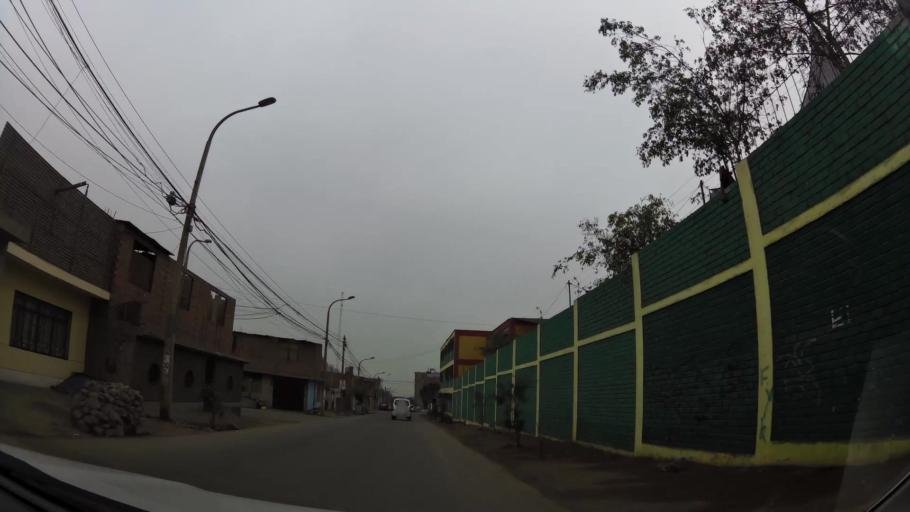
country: PE
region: Lima
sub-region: Lima
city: Urb. Santo Domingo
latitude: -11.9382
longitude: -76.9703
